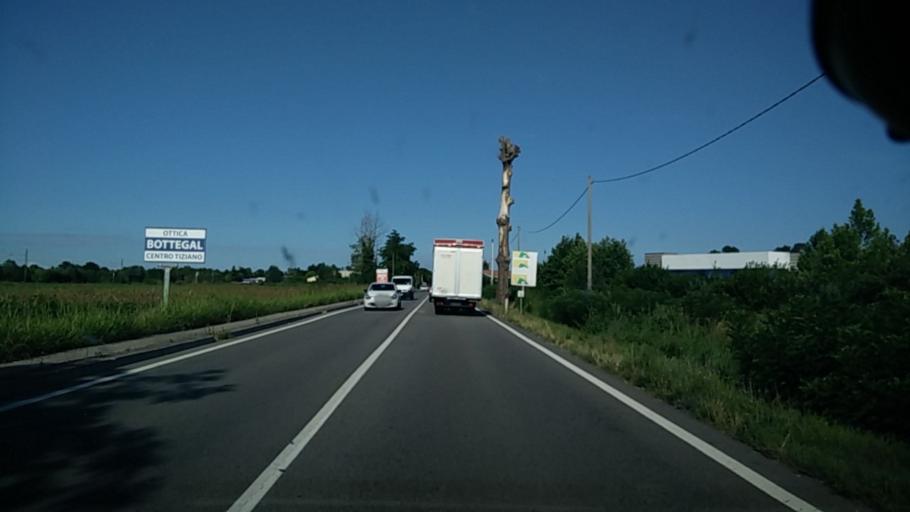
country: IT
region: Veneto
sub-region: Provincia di Treviso
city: San Floriano-Olmi
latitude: 45.6810
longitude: 12.3506
